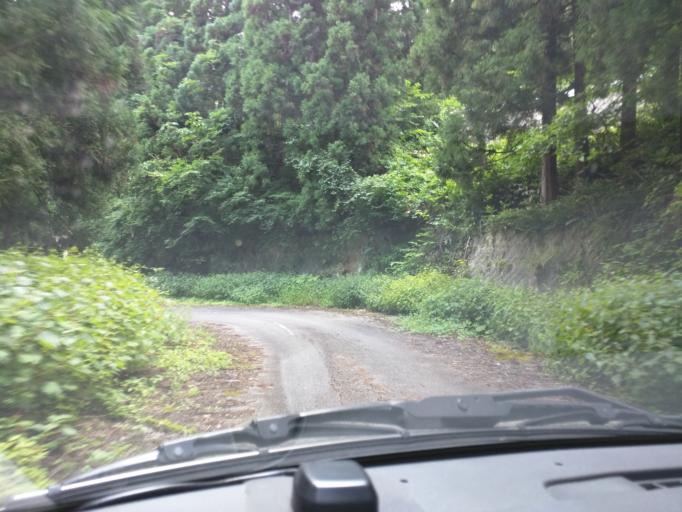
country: JP
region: Fukushima
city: Inawashiro
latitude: 37.4116
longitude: 140.0520
